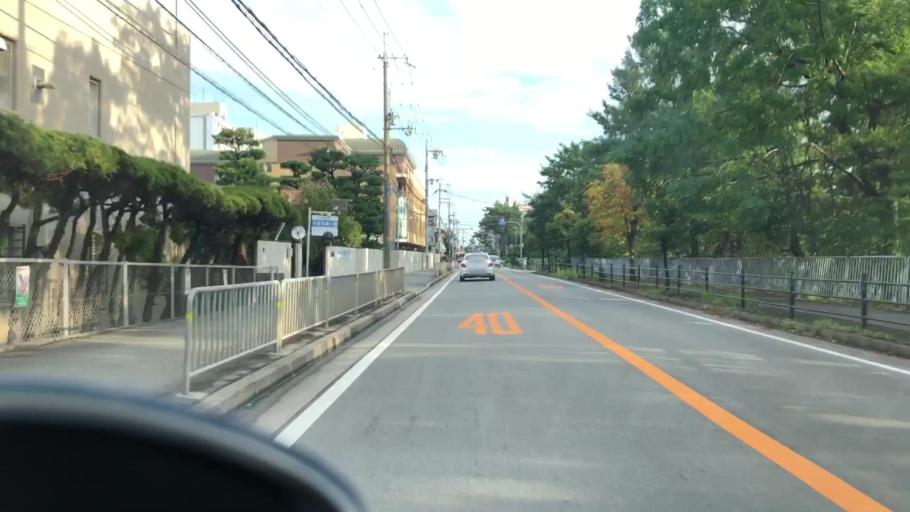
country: JP
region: Hyogo
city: Takarazuka
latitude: 34.7782
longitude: 135.3712
